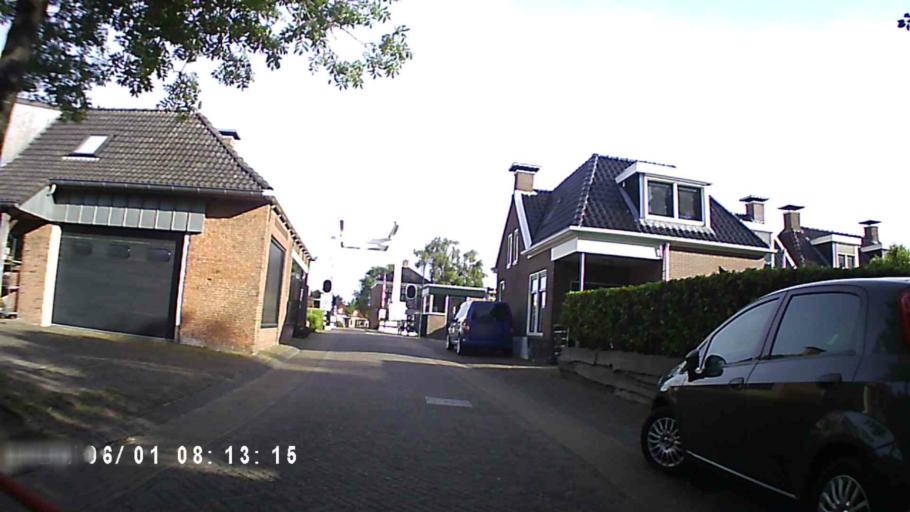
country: NL
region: Friesland
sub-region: Gemeente Ferwerderadiel
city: Burdaard
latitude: 53.2947
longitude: 5.8800
